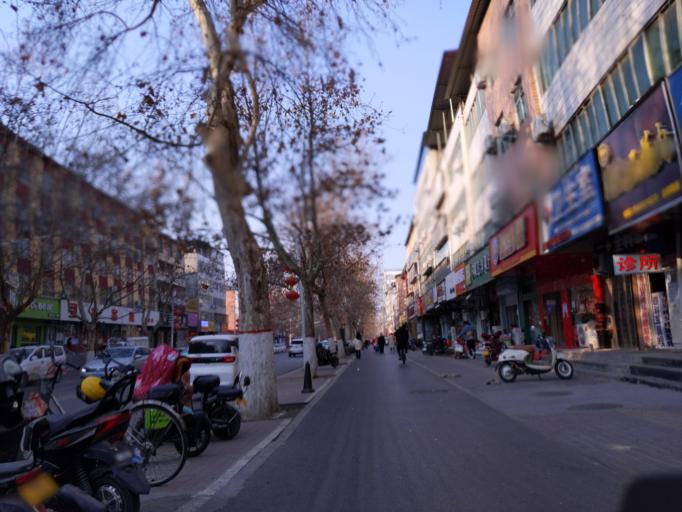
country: CN
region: Henan Sheng
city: Puyang
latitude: 35.7664
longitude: 115.0325
